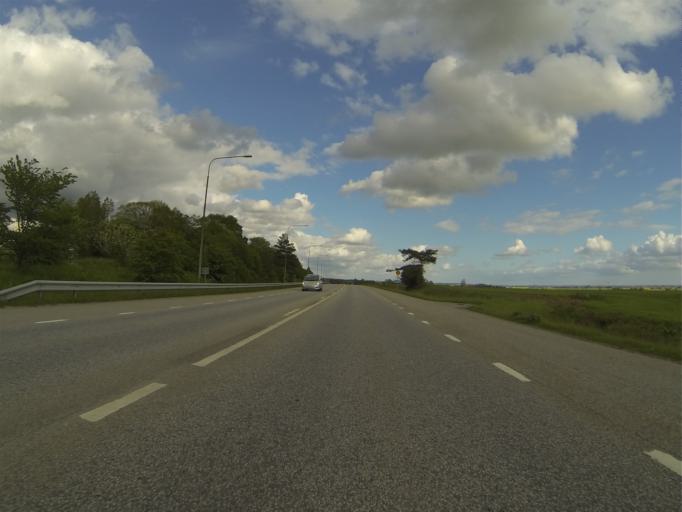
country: SE
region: Skane
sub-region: Lunds Kommun
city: Lund
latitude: 55.6891
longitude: 13.2512
